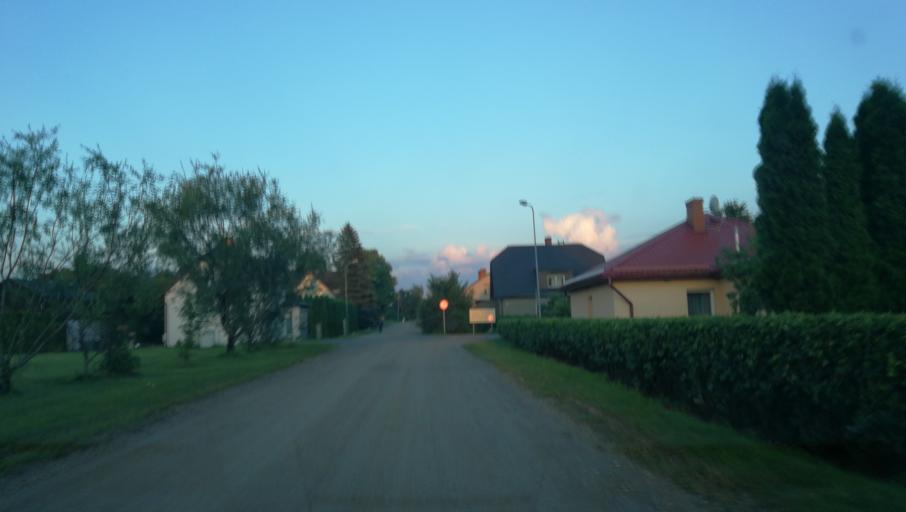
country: LV
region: Cesu Rajons
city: Cesis
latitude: 57.3194
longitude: 25.2923
